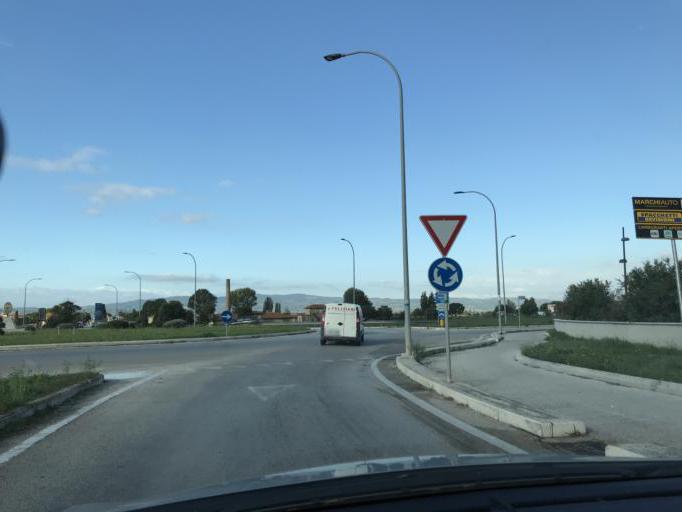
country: IT
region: Umbria
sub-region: Provincia di Perugia
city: Foligno
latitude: 42.9623
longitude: 12.6836
